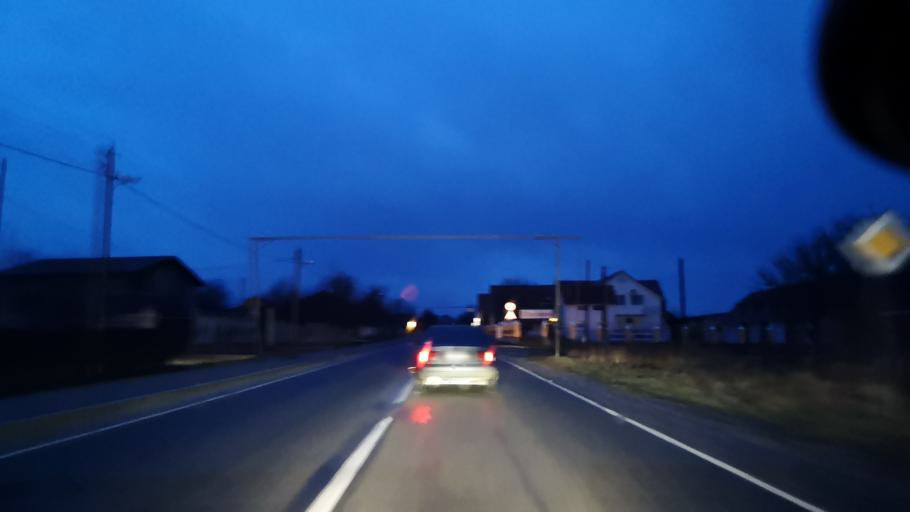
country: MD
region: Orhei
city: Orhei
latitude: 47.4330
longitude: 28.7992
